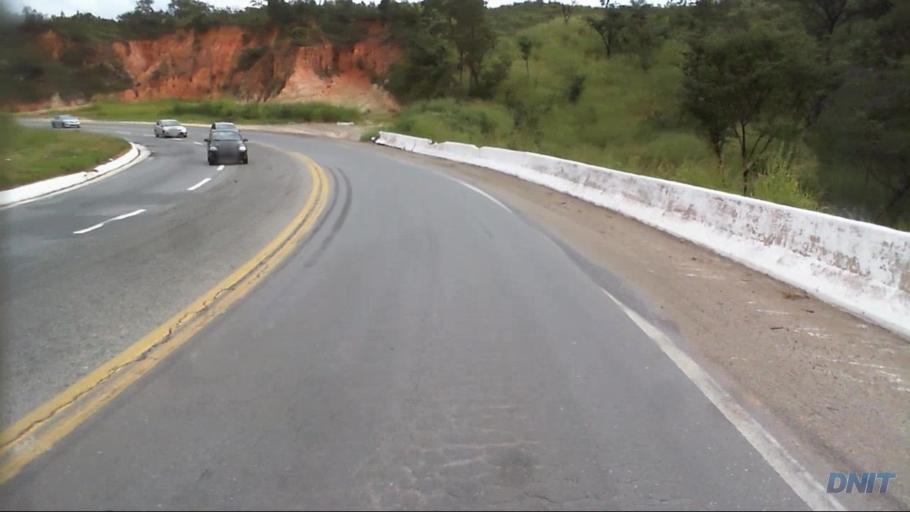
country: BR
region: Minas Gerais
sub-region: Caete
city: Caete
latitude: -19.7850
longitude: -43.7225
